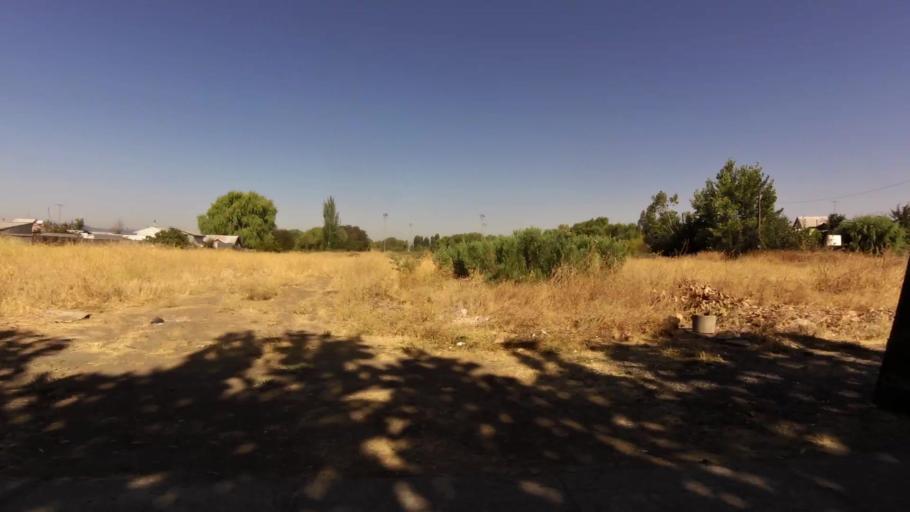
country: CL
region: Maule
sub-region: Provincia de Curico
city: Curico
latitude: -35.0009
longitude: -71.2459
